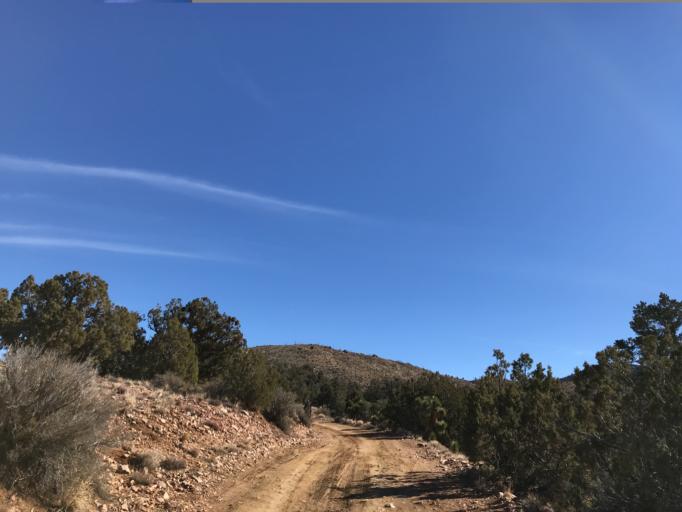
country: US
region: California
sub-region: San Bernardino County
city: Big Bear City
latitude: 34.2559
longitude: -116.7423
